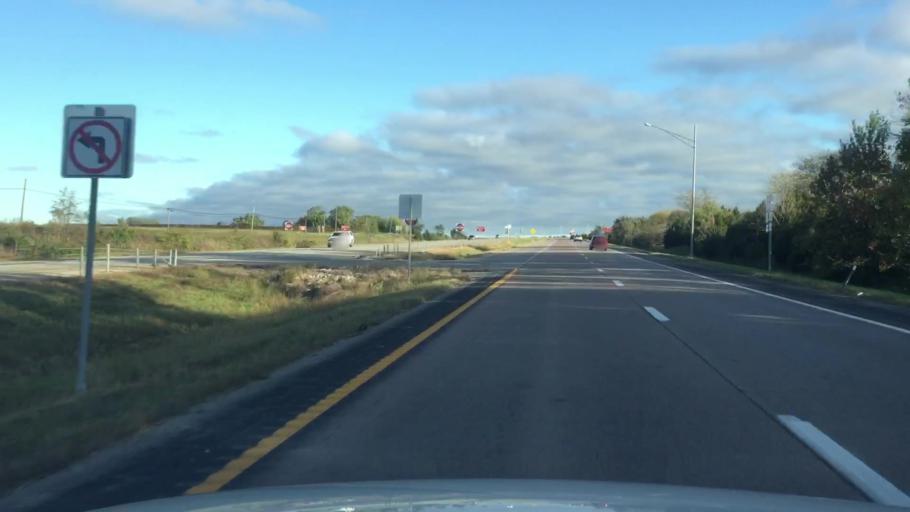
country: US
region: Missouri
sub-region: Boone County
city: Ashland
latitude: 38.8552
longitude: -92.2491
